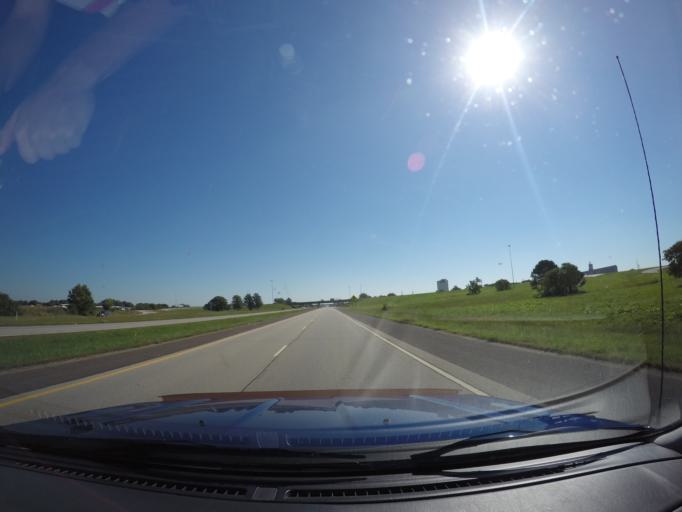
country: US
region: Kansas
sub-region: Shawnee County
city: Topeka
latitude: 39.0905
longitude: -95.7318
